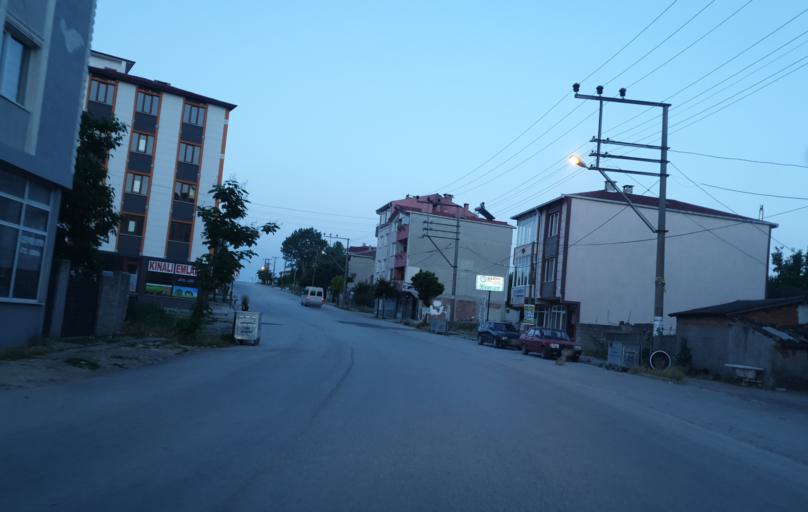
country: TR
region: Tekirdag
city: Saray
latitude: 41.3726
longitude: 27.9310
